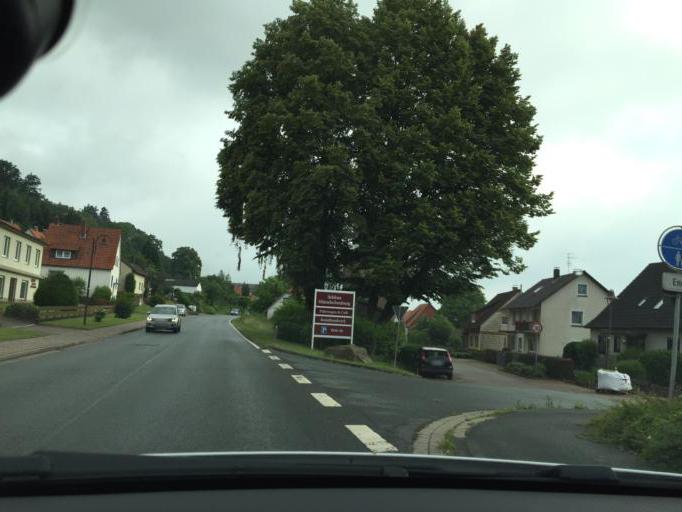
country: DE
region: Lower Saxony
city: Hameln
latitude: 52.0234
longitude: 9.3422
